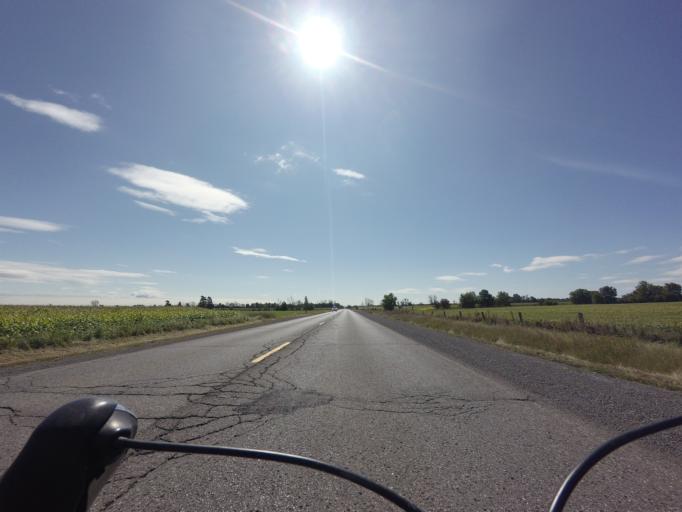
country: CA
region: Ontario
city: Bells Corners
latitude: 45.2176
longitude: -75.8299
